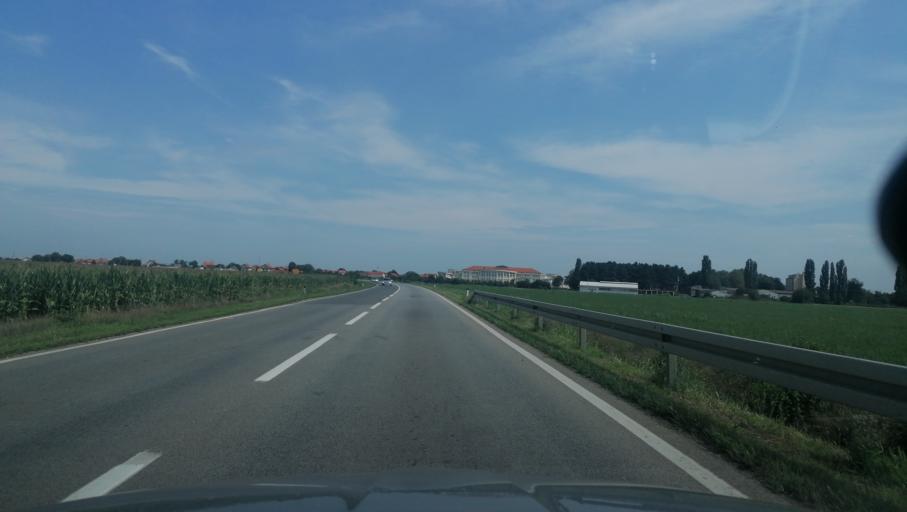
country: BA
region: Republika Srpska
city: Bijeljina
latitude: 44.7757
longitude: 19.2161
